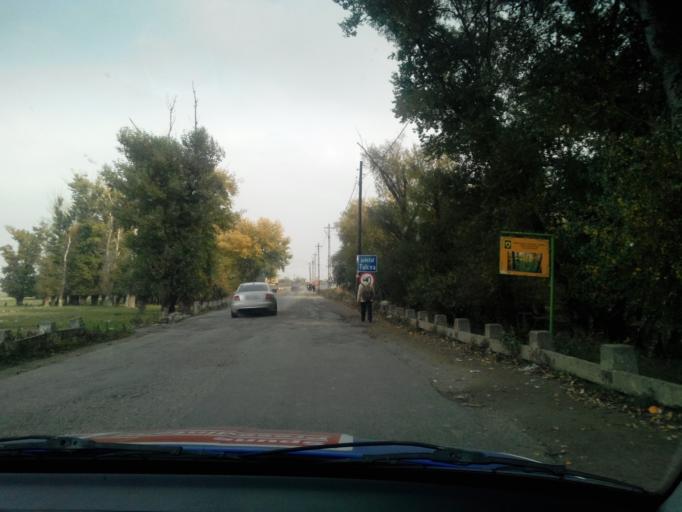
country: RO
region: Galati
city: Galati
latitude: 45.4101
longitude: 28.0447
